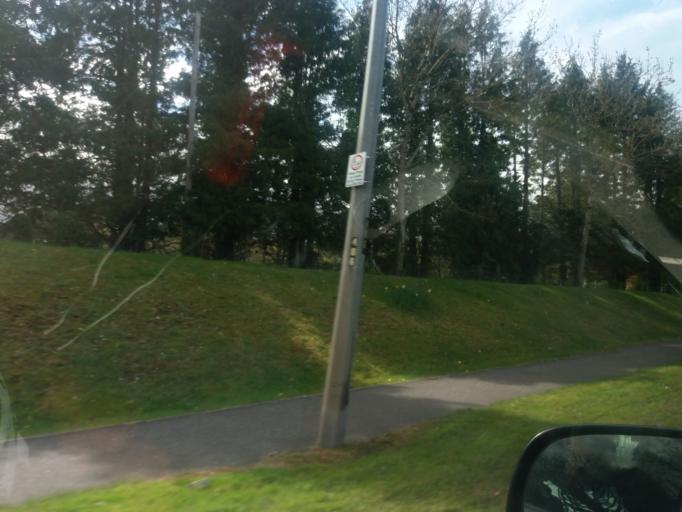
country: GB
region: Northern Ireland
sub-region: Fermanagh District
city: Enniskillen
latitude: 54.3565
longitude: -7.6687
